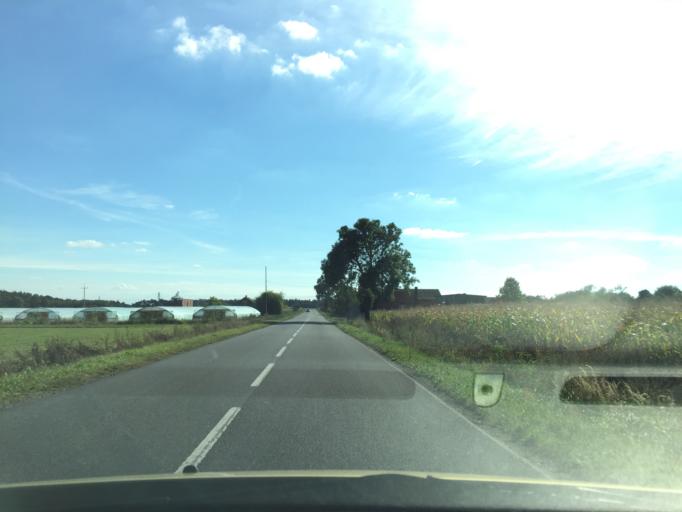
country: PL
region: Greater Poland Voivodeship
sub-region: Powiat kaliski
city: Stawiszyn
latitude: 51.9343
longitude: 18.1480
